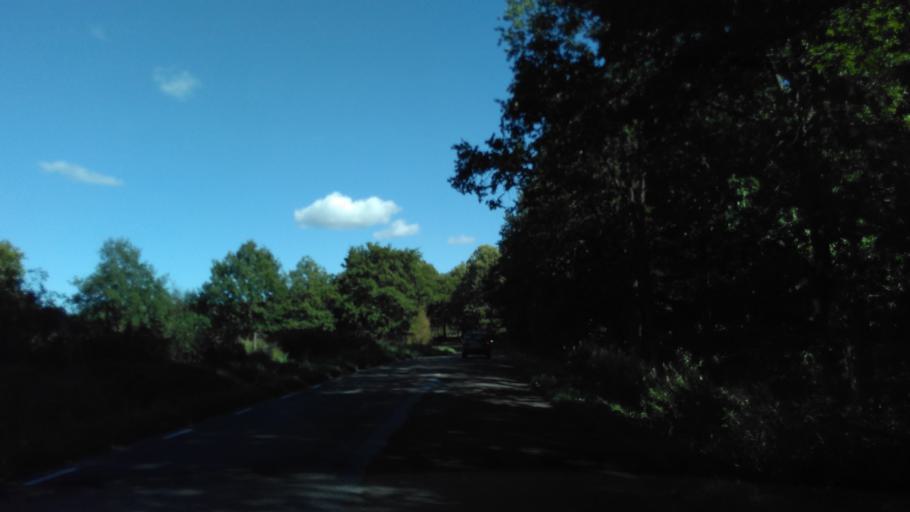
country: SE
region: Vaestra Goetaland
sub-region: Skara Kommun
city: Axvall
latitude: 58.4422
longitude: 13.6570
